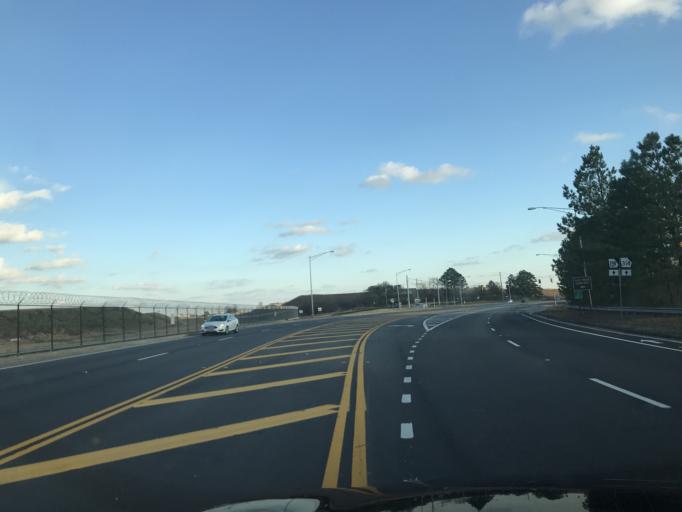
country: US
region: Georgia
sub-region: Fulton County
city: College Park
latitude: 33.6297
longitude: -84.4495
